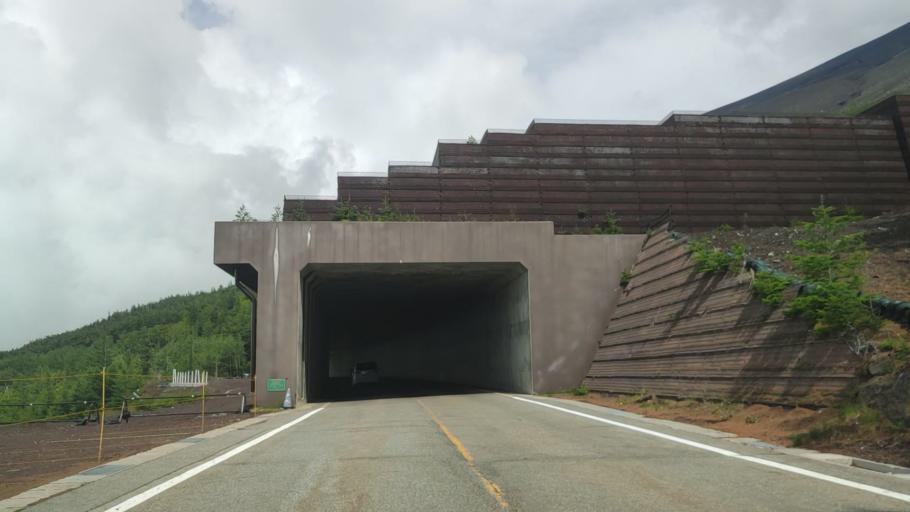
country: JP
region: Yamanashi
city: Fujikawaguchiko
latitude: 35.3907
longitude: 138.7163
